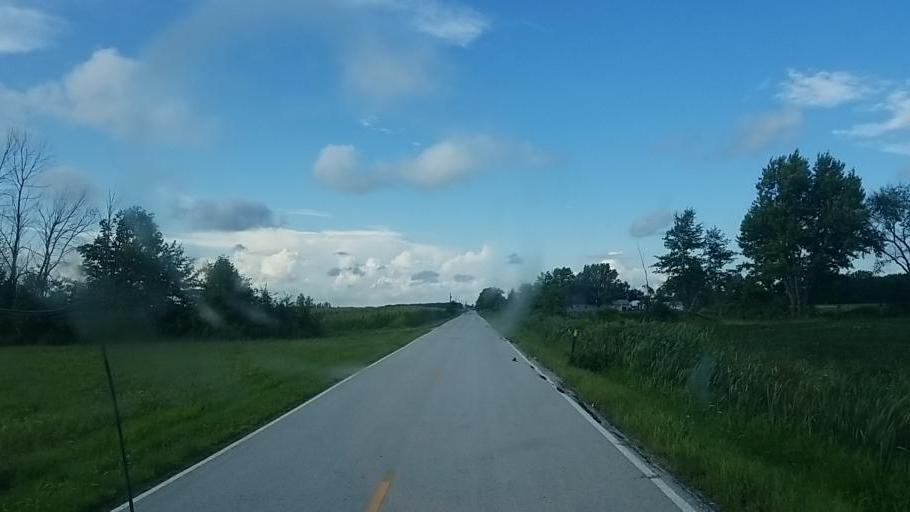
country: US
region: Ohio
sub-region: Hardin County
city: Forest
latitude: 40.7518
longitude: -83.4966
